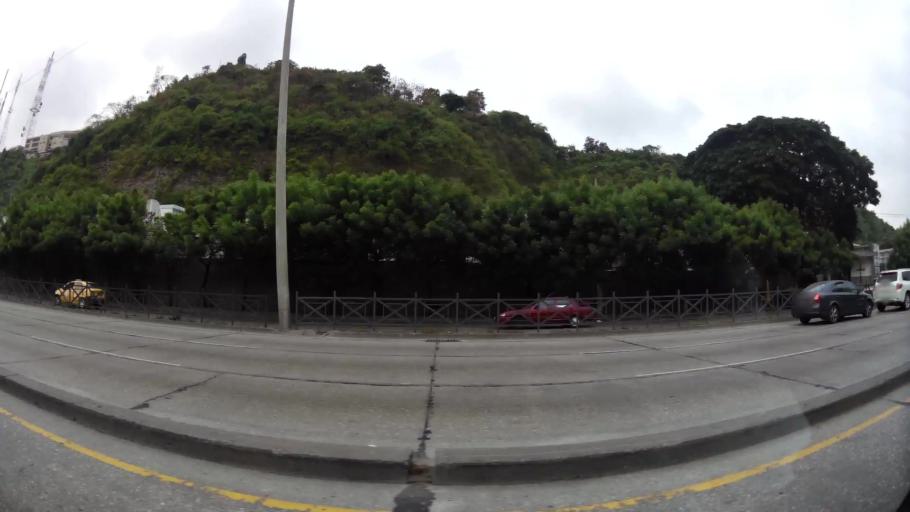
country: EC
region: Guayas
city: Eloy Alfaro
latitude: -2.1788
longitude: -79.8850
